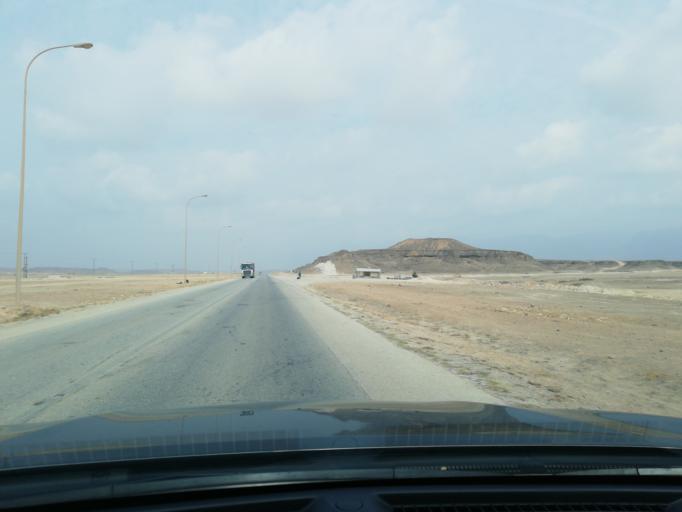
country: OM
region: Zufar
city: Salalah
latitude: 16.9516
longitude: 53.9301
